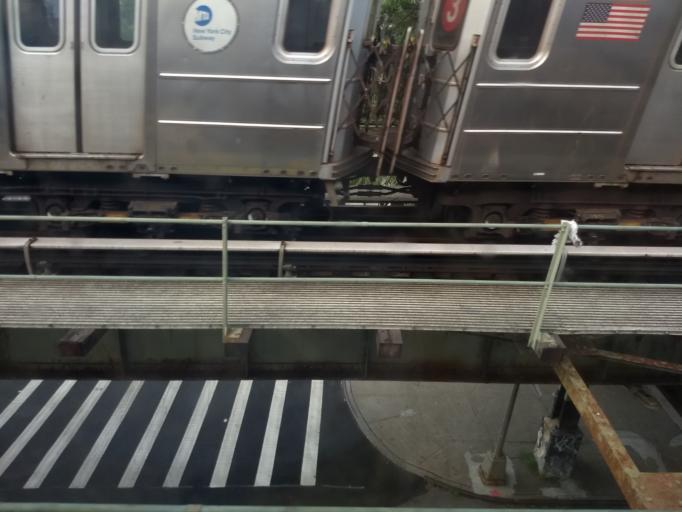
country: US
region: New York
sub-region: Kings County
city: East New York
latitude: 40.6624
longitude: -73.9107
